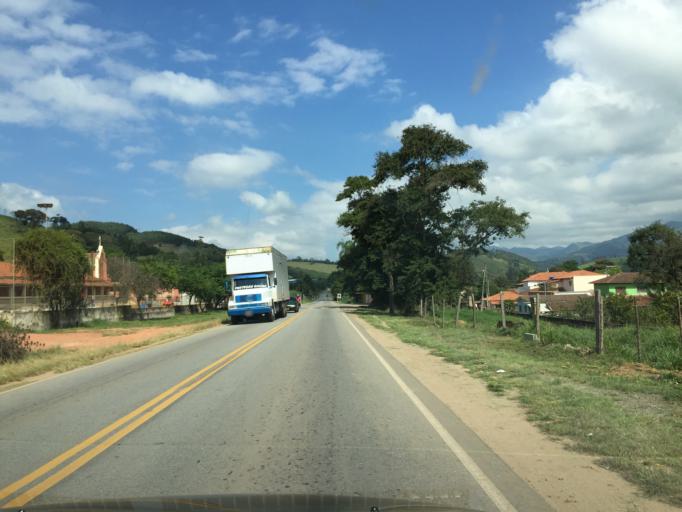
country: BR
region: Minas Gerais
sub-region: Passa Quatro
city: Passa Quatro
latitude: -22.3567
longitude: -44.9508
